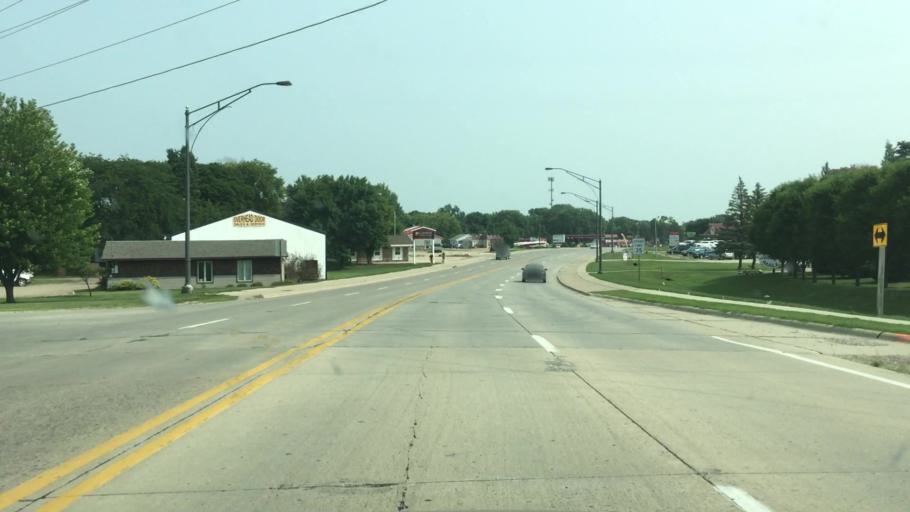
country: US
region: Iowa
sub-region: Dickinson County
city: Arnolds Park
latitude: 43.3602
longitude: -95.1413
